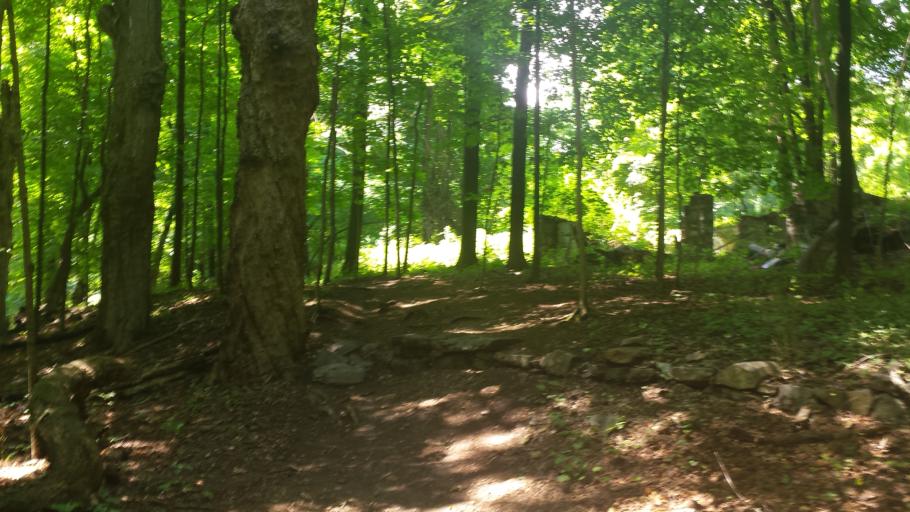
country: US
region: New York
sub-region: Westchester County
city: Thornwood
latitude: 41.1182
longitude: -73.7882
